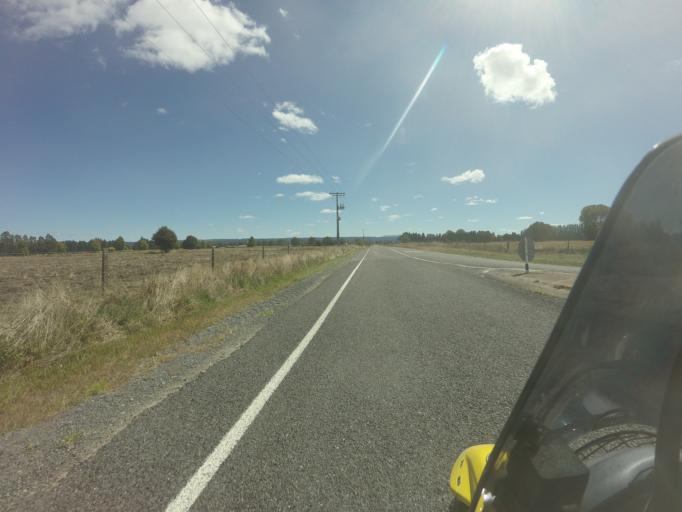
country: NZ
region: Bay of Plenty
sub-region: Whakatane District
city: Murupara
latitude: -38.4670
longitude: 176.7561
